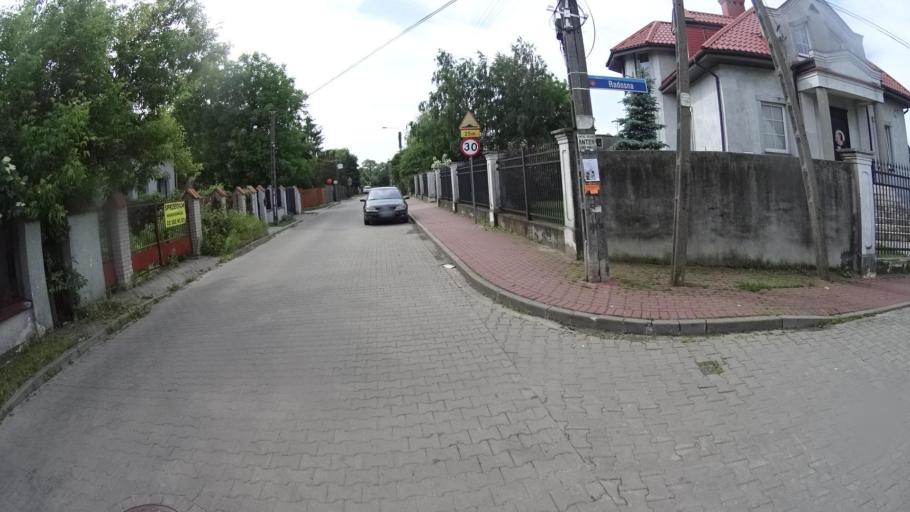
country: PL
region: Masovian Voivodeship
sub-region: Powiat pruszkowski
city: Piastow
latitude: 52.1963
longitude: 20.8511
